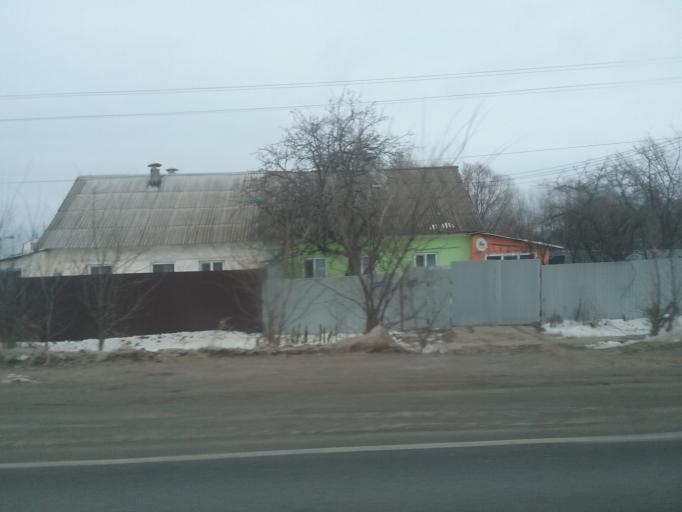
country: RU
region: Tula
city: Bolokhovo
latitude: 54.0520
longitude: 37.8174
